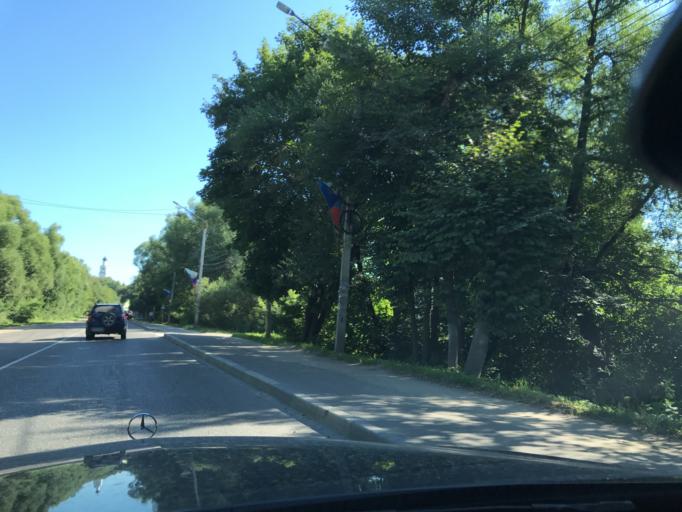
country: RU
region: Vladimir
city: Kirzhach
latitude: 56.1567
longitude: 38.8636
